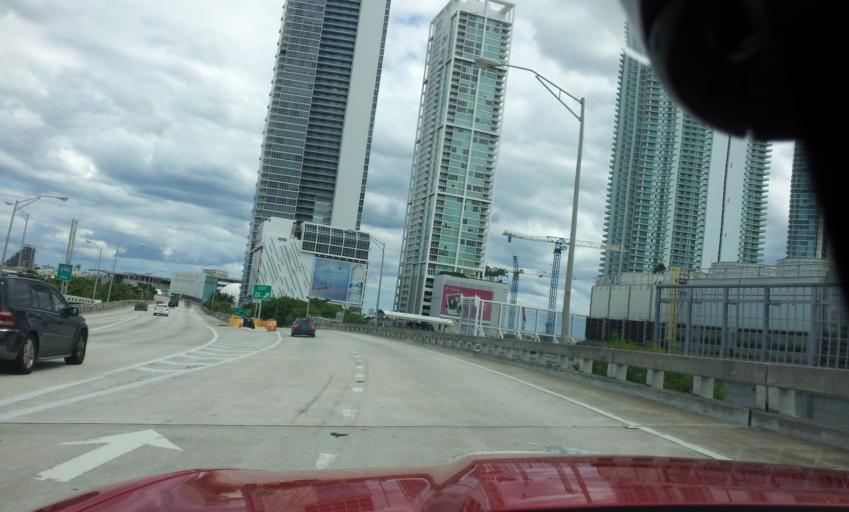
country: US
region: Florida
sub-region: Miami-Dade County
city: Miami
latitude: 25.7858
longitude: -80.1944
